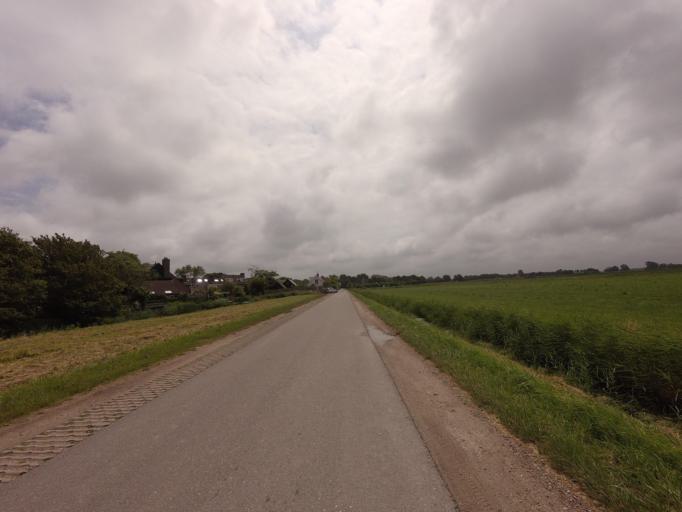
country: NL
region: North Holland
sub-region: Gemeente Schagen
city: Schagen
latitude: 52.7868
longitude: 4.7729
